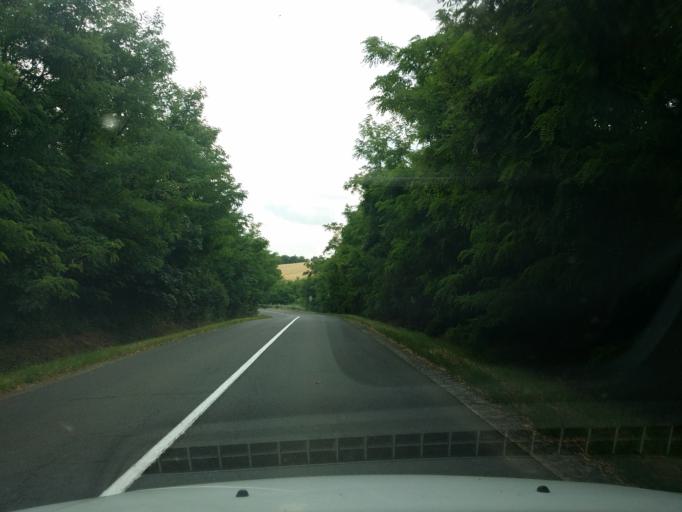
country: HU
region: Nograd
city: Bercel
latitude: 47.9336
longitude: 19.3668
